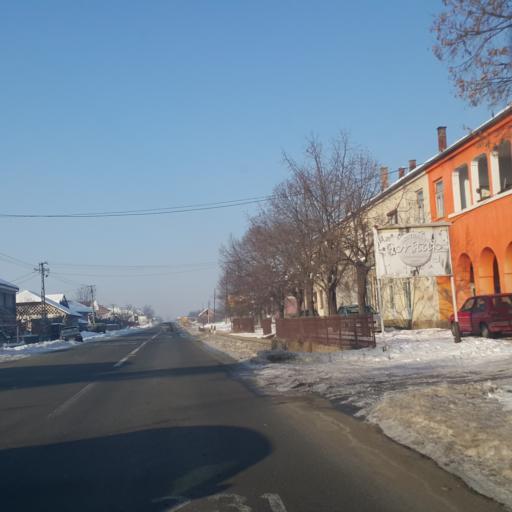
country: RS
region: Central Serbia
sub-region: Toplicki Okrug
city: Prokuplje
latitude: 43.2416
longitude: 21.4825
